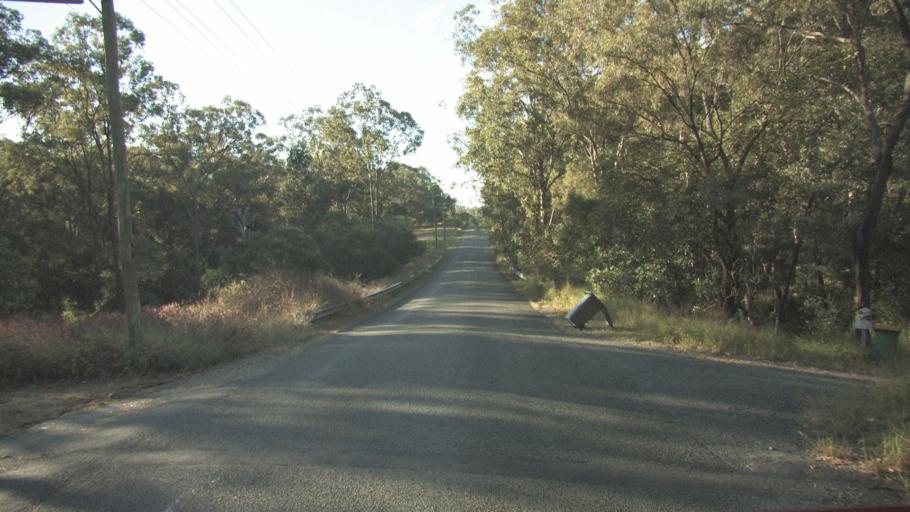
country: AU
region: Queensland
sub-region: Logan
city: Waterford West
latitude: -27.7289
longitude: 153.1524
